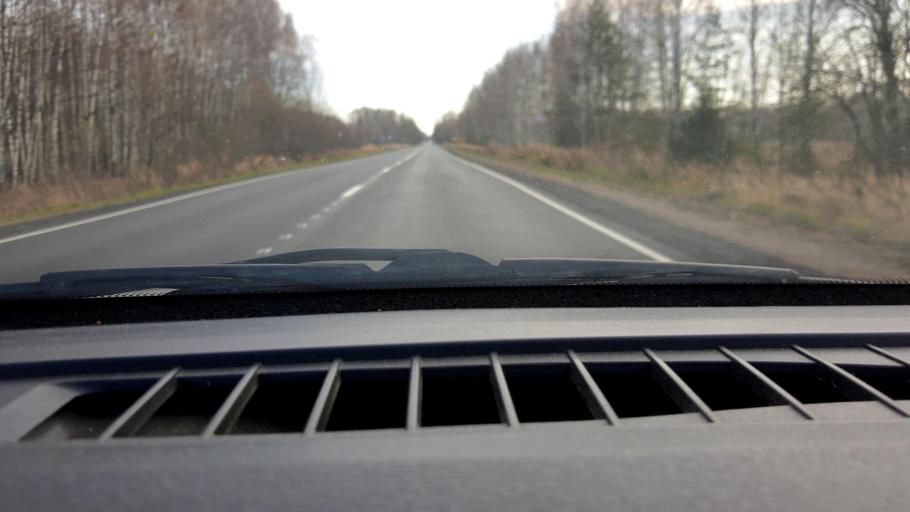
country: RU
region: Nizjnij Novgorod
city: Novaya Balakhna
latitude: 56.5709
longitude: 43.7097
